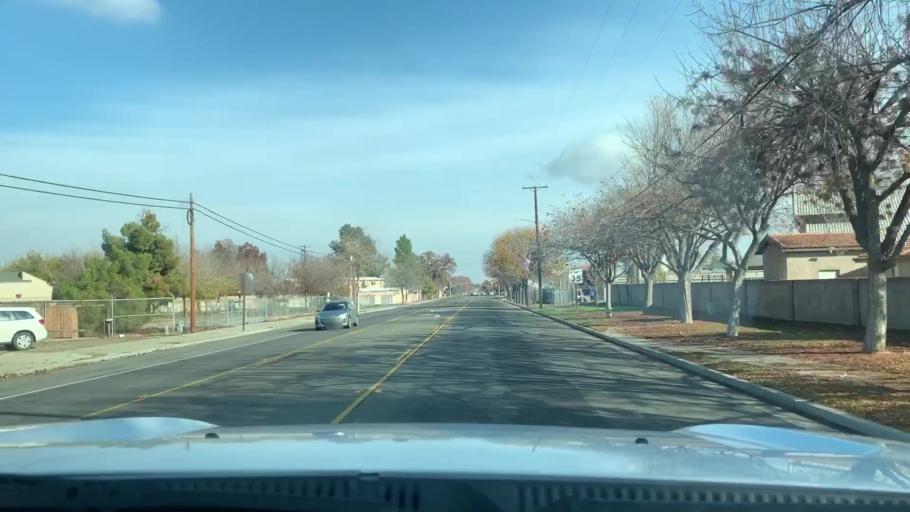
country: US
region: California
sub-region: Fresno County
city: Coalinga
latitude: 36.1332
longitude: -120.3665
